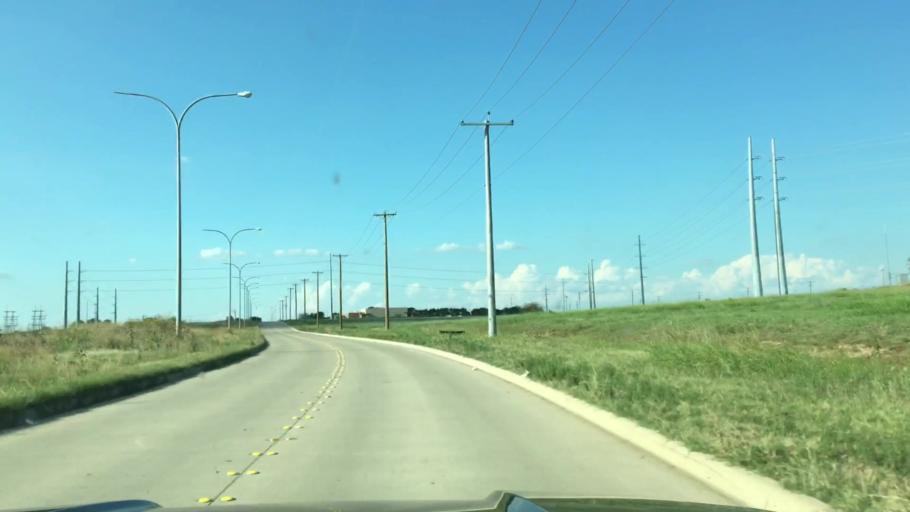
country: US
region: Texas
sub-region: Tarrant County
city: Haslet
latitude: 32.9939
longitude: -97.3590
